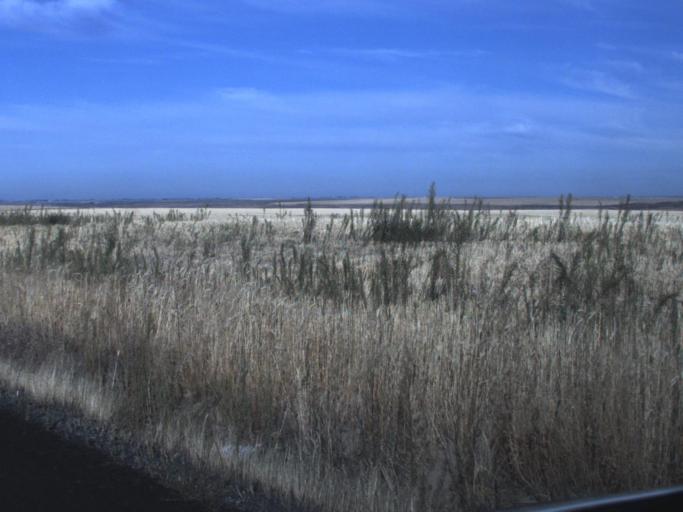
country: US
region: Washington
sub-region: Franklin County
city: Connell
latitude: 46.6203
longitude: -118.6713
